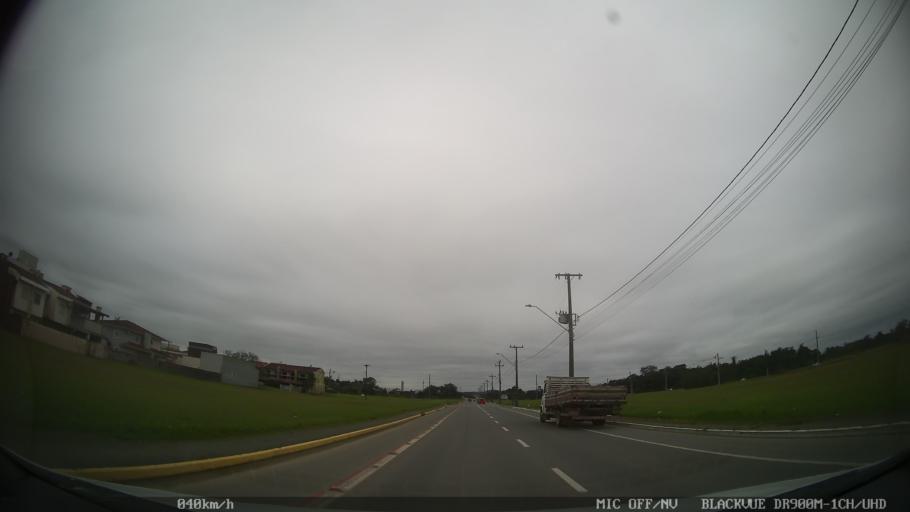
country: BR
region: Santa Catarina
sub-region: Joinville
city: Joinville
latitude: -26.2921
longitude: -48.9189
